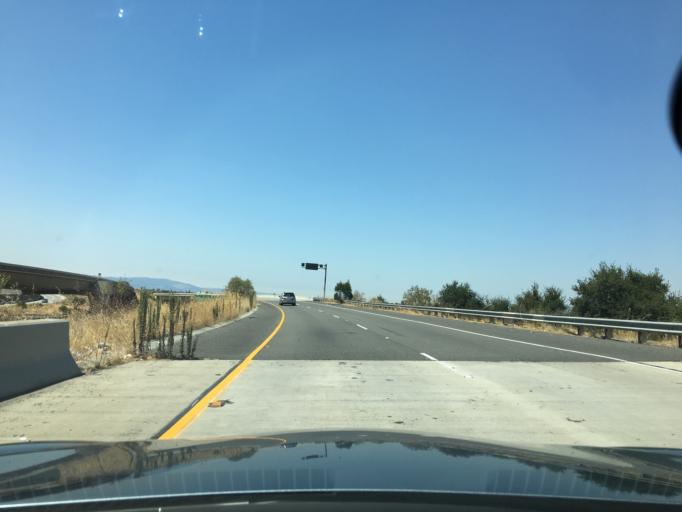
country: US
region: California
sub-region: Santa Clara County
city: Seven Trees
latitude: 37.2412
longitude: -121.7664
